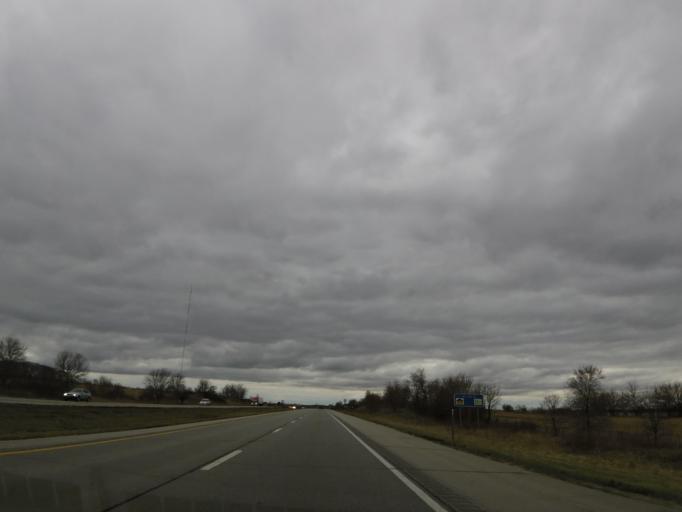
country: US
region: Iowa
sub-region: Linn County
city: Robins
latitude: 42.0694
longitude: -91.7008
